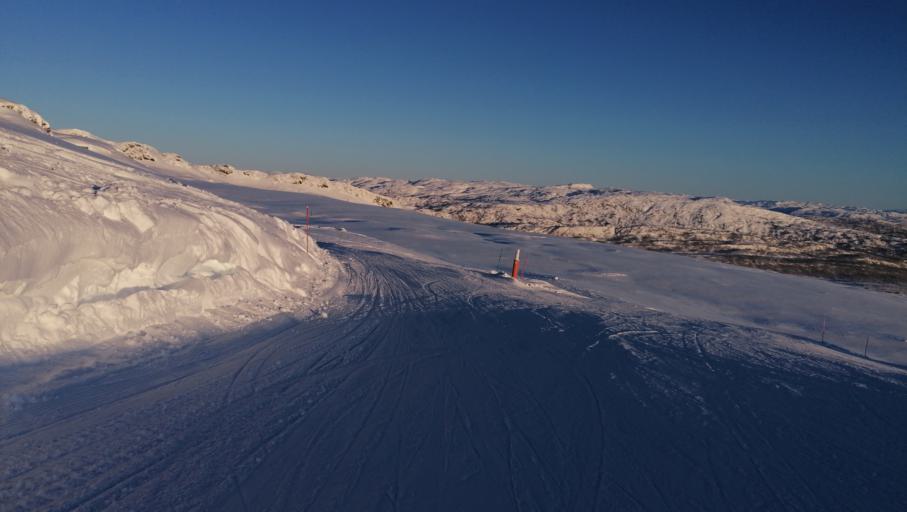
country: NO
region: Aust-Agder
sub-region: Bykle
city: Hovden
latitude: 59.5815
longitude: 7.3319
